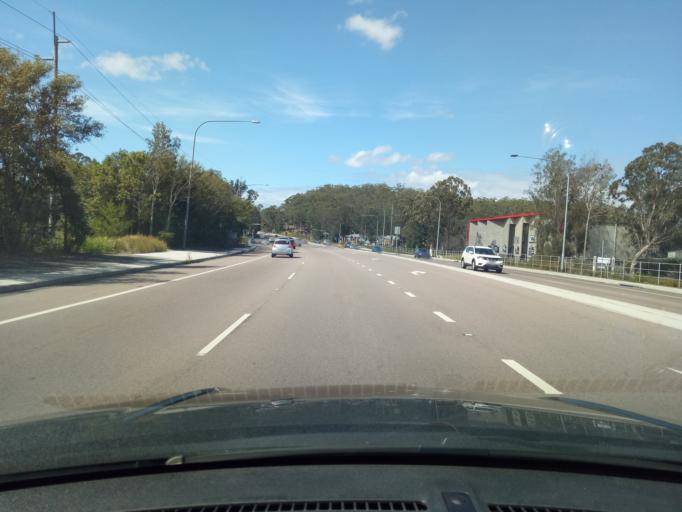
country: AU
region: New South Wales
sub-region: Wyong Shire
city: Chittaway Bay
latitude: -33.3263
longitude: 151.4280
